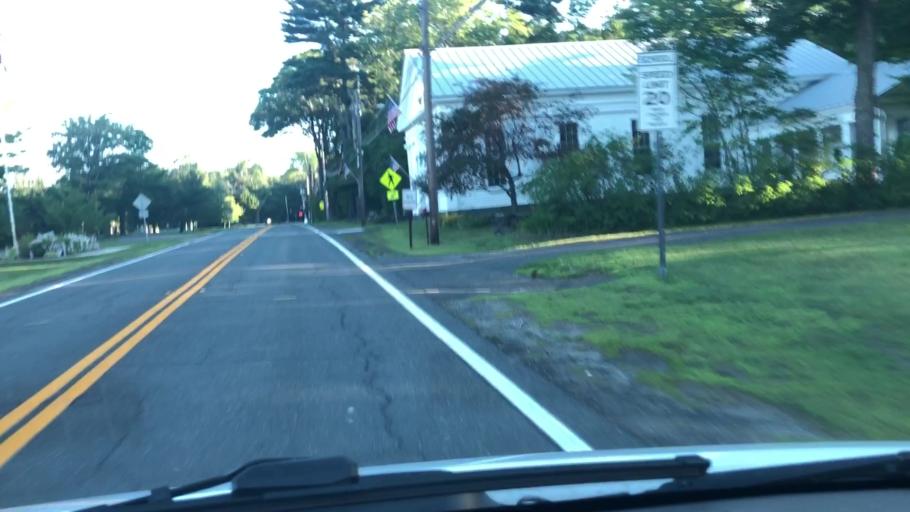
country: US
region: Massachusetts
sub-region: Hampshire County
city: Chesterfield
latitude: 42.3991
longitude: -72.9371
